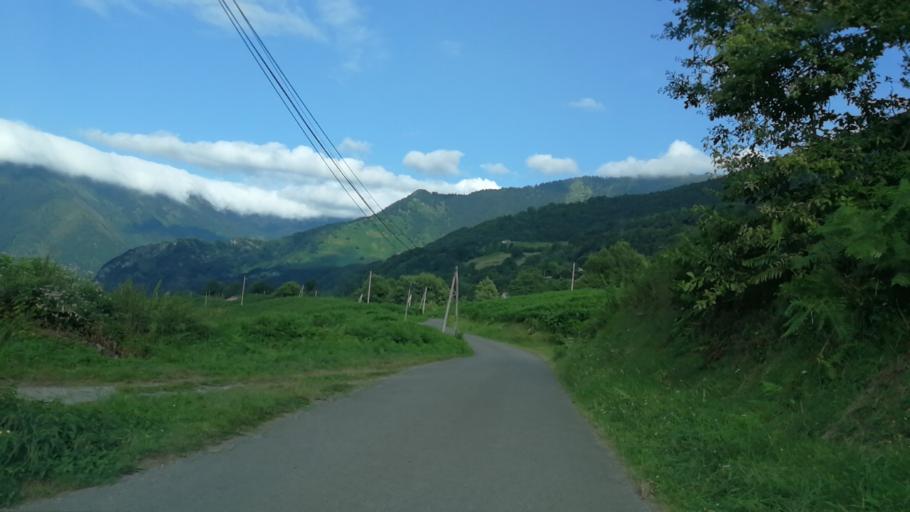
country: FR
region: Aquitaine
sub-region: Departement des Pyrenees-Atlantiques
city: Arette
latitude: 42.9237
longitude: -0.6483
